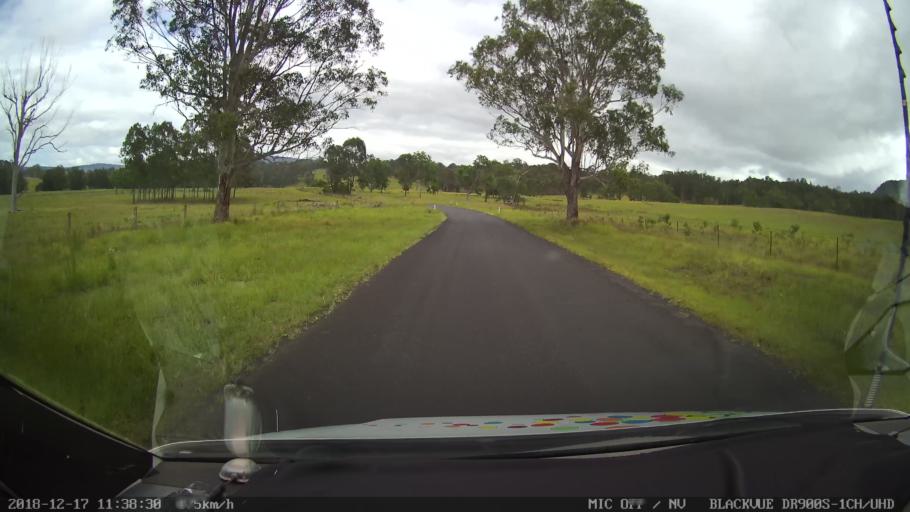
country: AU
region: New South Wales
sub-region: Kyogle
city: Kyogle
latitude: -28.6947
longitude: 152.5997
